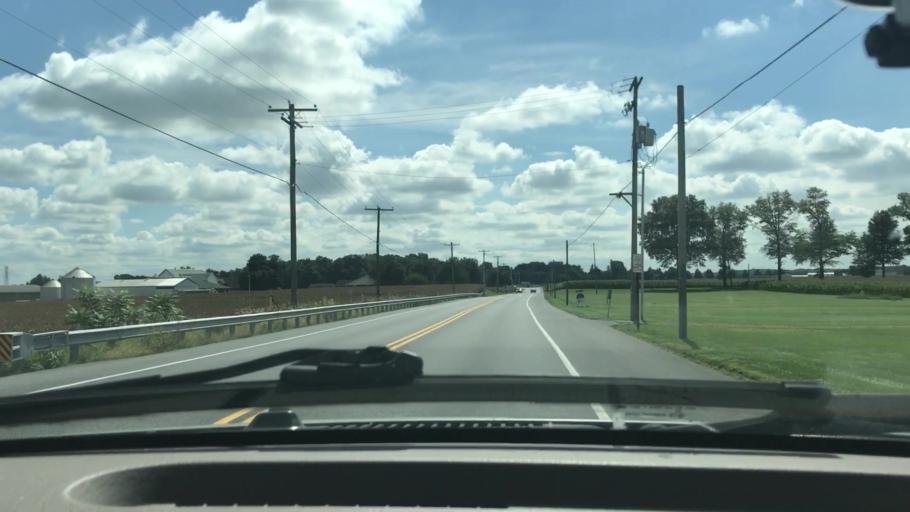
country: US
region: Pennsylvania
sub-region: Lancaster County
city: Manheim
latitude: 40.1314
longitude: -76.3805
